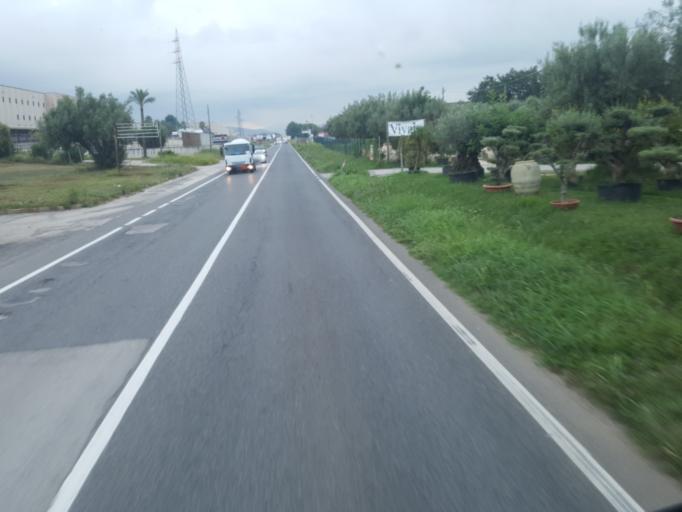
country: IT
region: Campania
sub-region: Provincia di Caserta
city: Pignataro Maggiore
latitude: 41.1665
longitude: 14.1570
